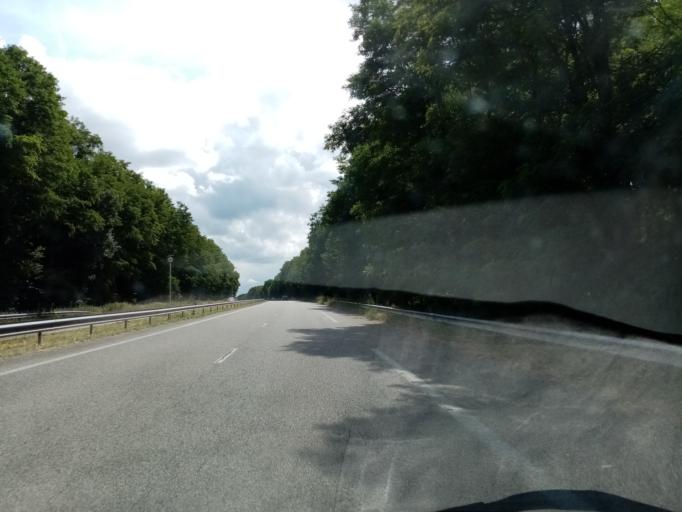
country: DE
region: Rheinland-Pfalz
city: Scheibenhardt
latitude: 48.9389
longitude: 8.1280
